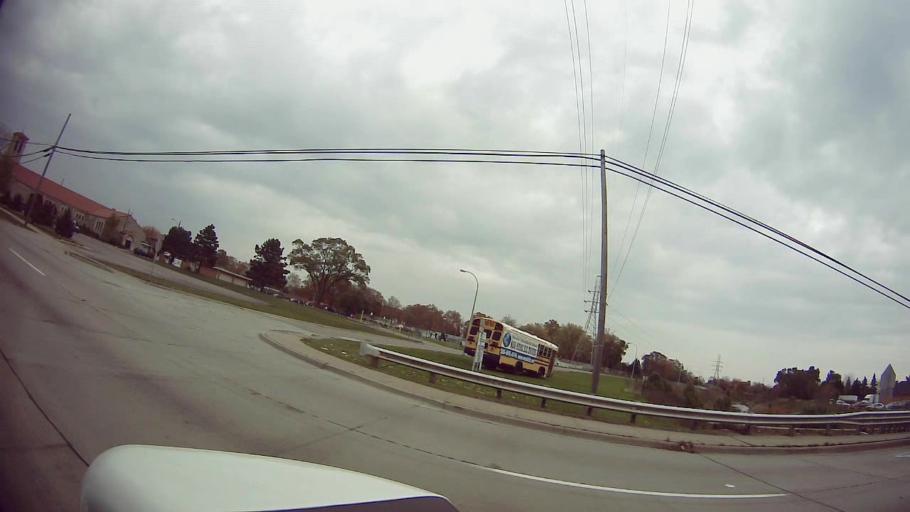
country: US
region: Michigan
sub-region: Macomb County
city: Center Line
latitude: 42.5292
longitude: -83.0475
